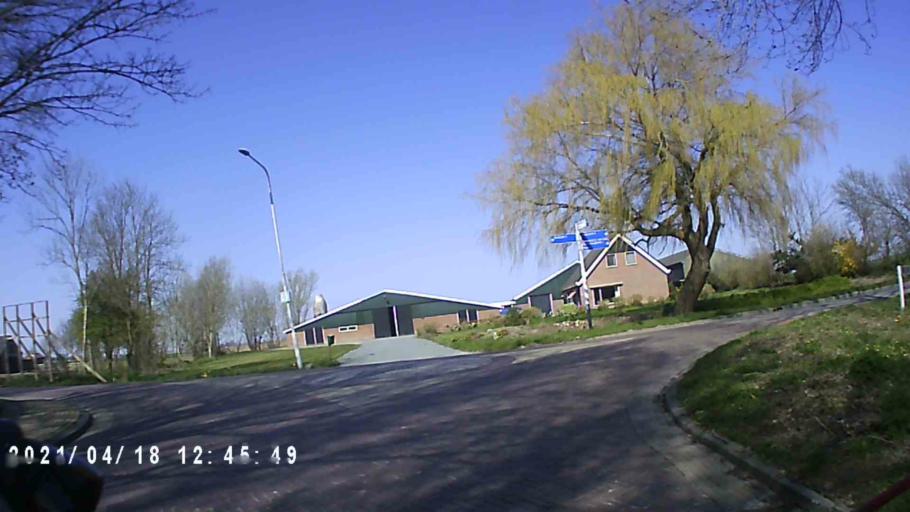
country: NL
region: Friesland
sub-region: Gemeente Dantumadiel
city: Walterswald
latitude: 53.3649
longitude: 6.0481
